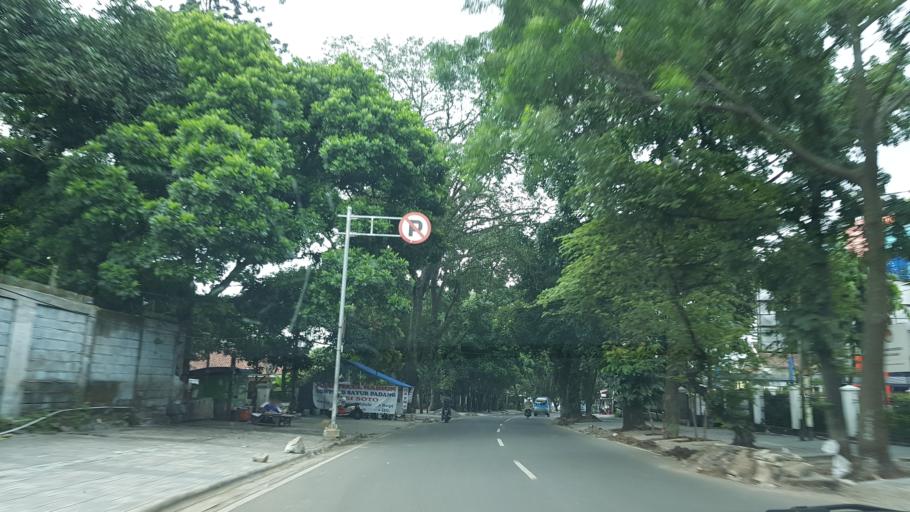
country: ID
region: West Java
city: Bandung
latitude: -6.8958
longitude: 107.6093
